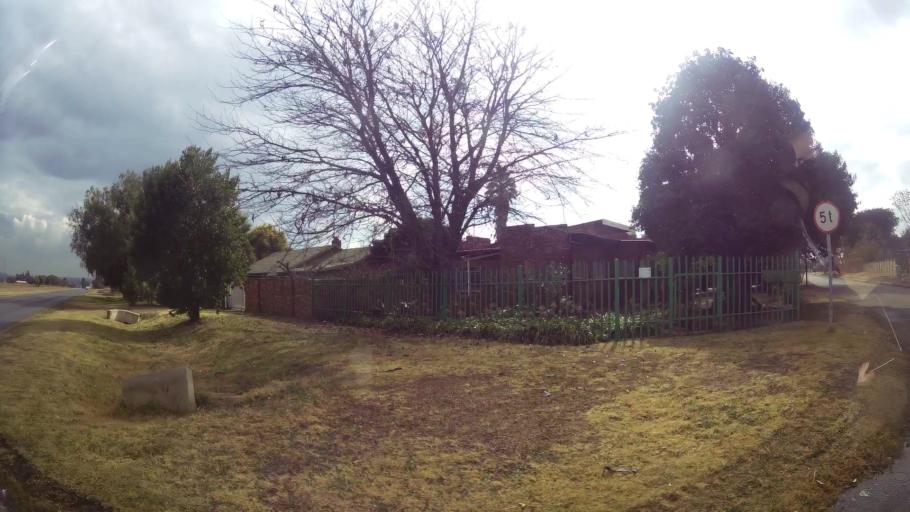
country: ZA
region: Gauteng
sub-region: Sedibeng District Municipality
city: Meyerton
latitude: -26.6016
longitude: 28.0380
